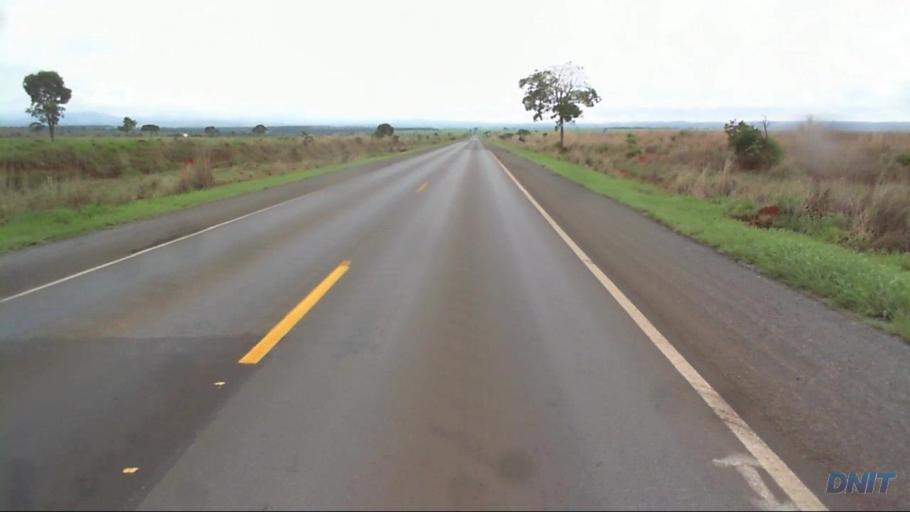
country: BR
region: Goias
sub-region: Padre Bernardo
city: Padre Bernardo
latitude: -15.1751
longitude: -48.4014
